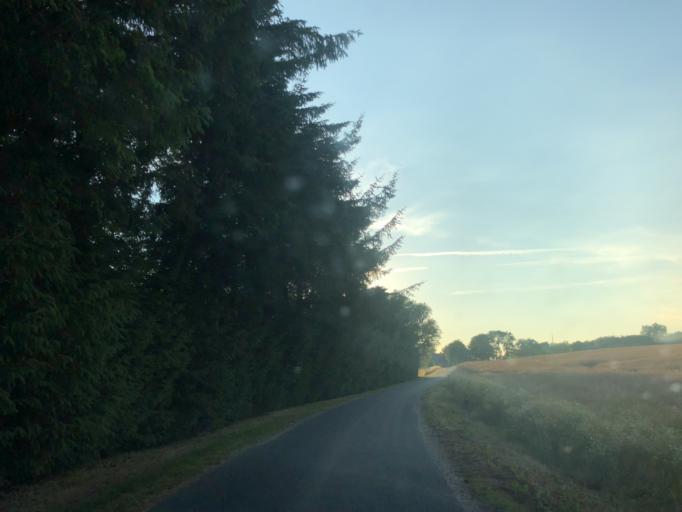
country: DK
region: Central Jutland
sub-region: Holstebro Kommune
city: Holstebro
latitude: 56.3696
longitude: 8.6791
